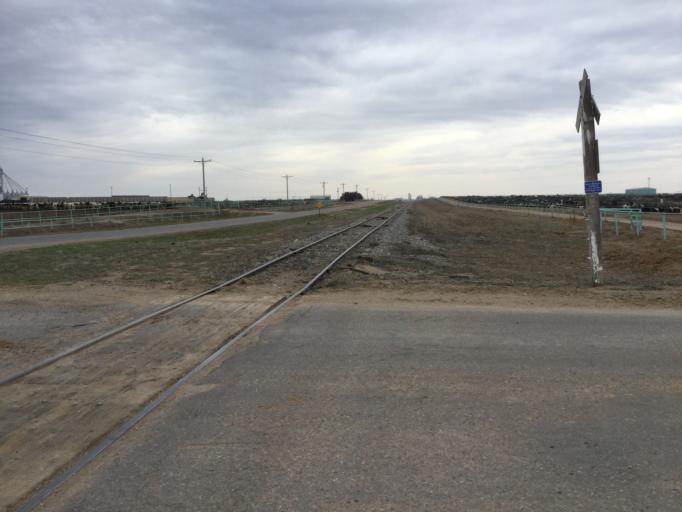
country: US
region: Kansas
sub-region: Stanton County
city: Johnson
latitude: 37.5627
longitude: -101.6897
